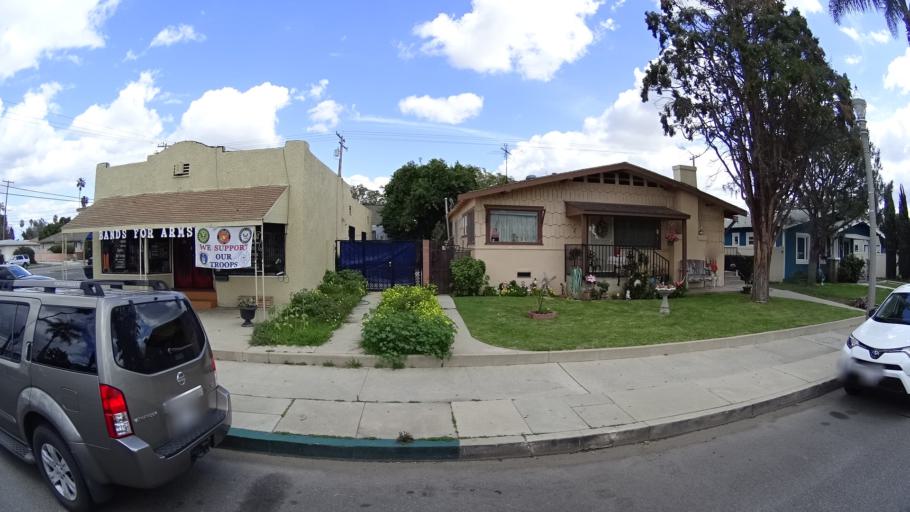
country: US
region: California
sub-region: Orange County
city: Anaheim
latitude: 33.8434
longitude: -117.9186
